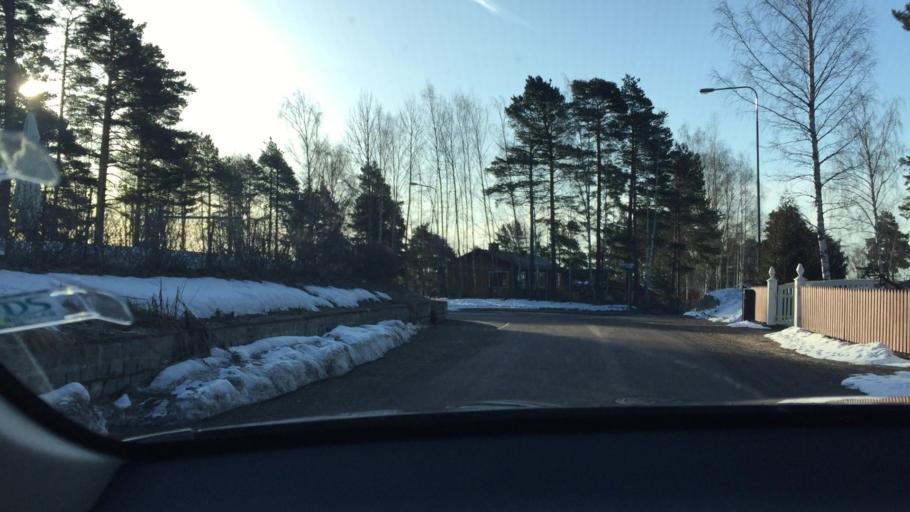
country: SE
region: Dalarna
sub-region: Faluns Kommun
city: Falun
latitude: 60.5705
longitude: 15.6488
